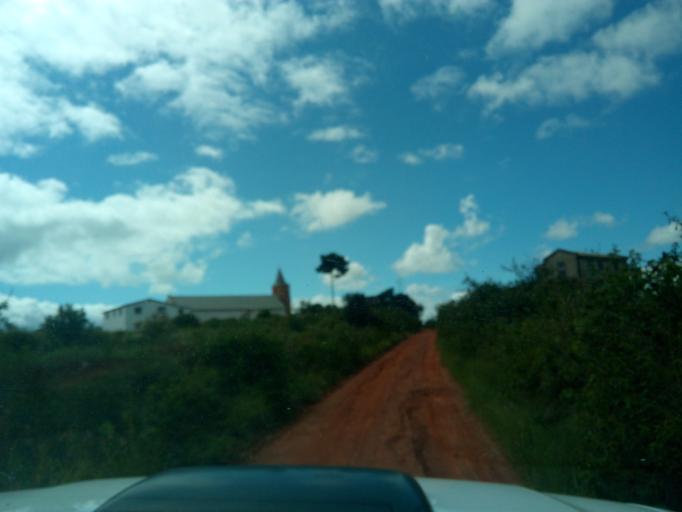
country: MG
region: Analamanga
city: Antananarivo
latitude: -18.7319
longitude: 47.4148
